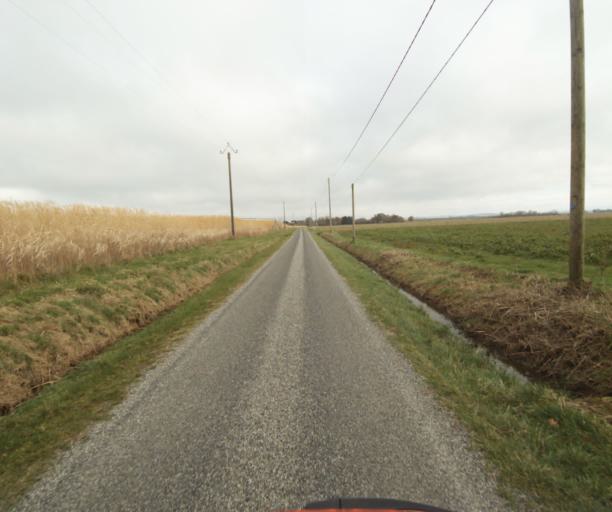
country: FR
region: Midi-Pyrenees
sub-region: Departement de l'Ariege
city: Mazeres
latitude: 43.1852
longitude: 1.6605
